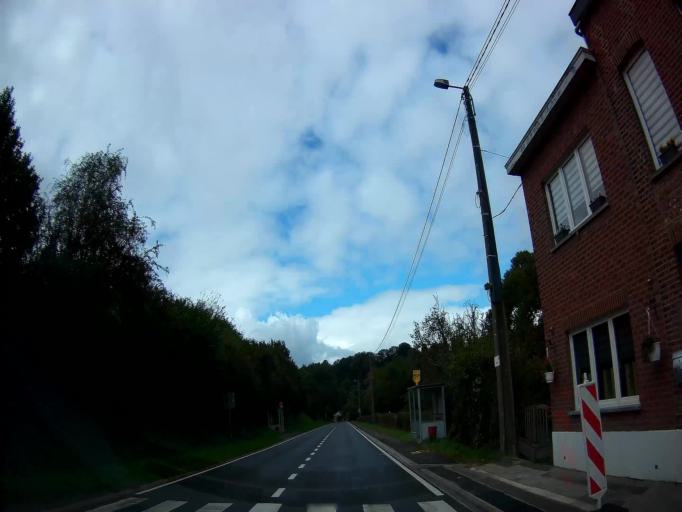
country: BE
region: Wallonia
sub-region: Province de Liege
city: Baelen
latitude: 50.6236
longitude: 5.9576
